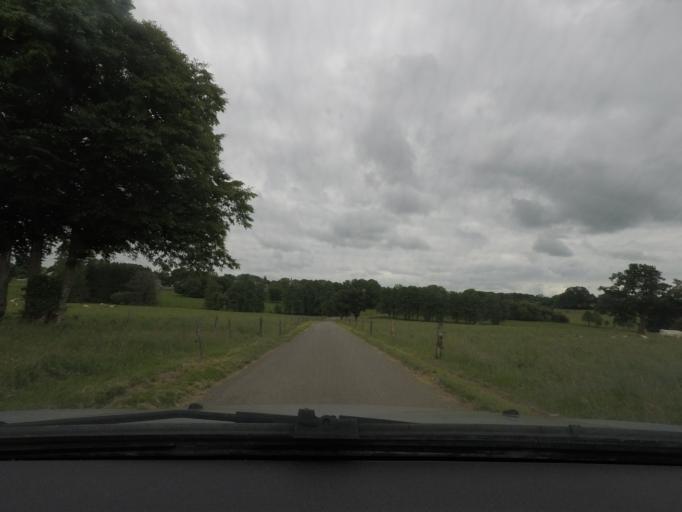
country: BE
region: Wallonia
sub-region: Province du Luxembourg
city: Leglise
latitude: 49.8353
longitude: 5.4926
